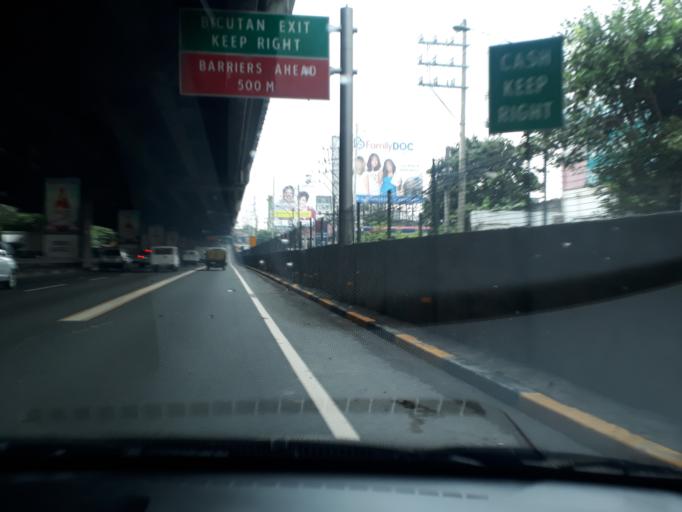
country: PH
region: Calabarzon
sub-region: Province of Rizal
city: Taguig
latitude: 14.4964
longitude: 121.0405
